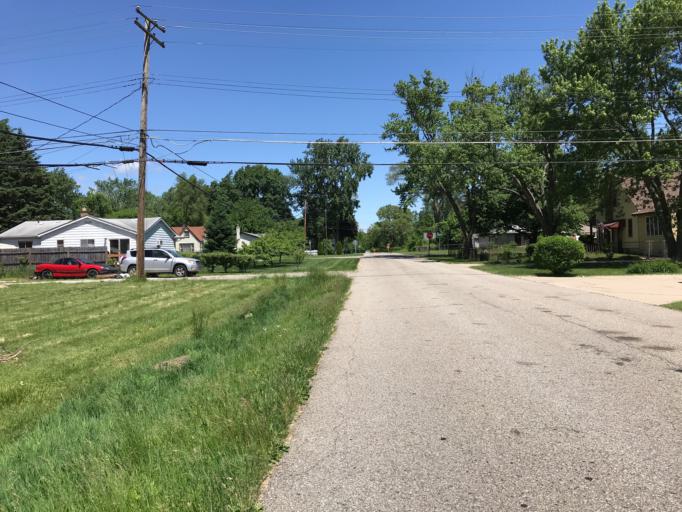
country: US
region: Michigan
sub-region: Oakland County
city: Southfield
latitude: 42.4742
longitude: -83.2373
